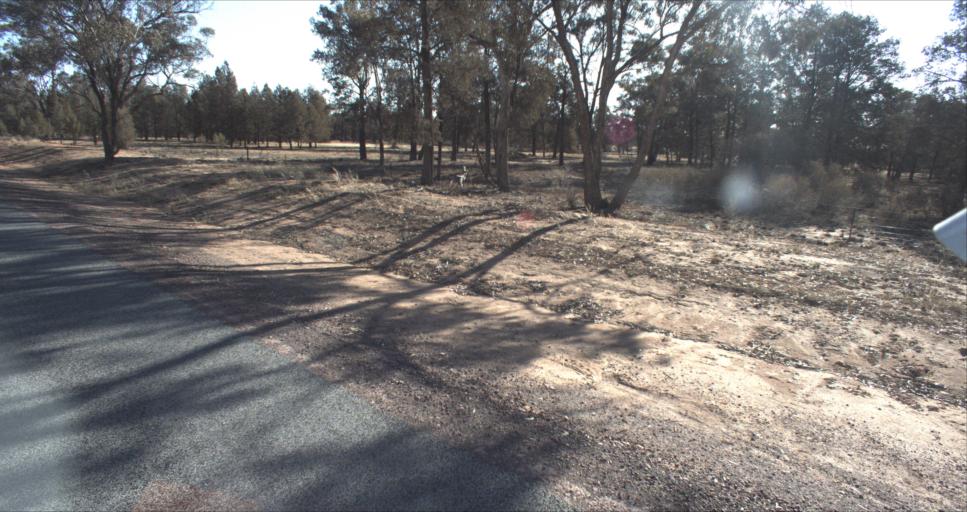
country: AU
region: New South Wales
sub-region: Leeton
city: Leeton
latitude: -34.6471
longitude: 146.3519
